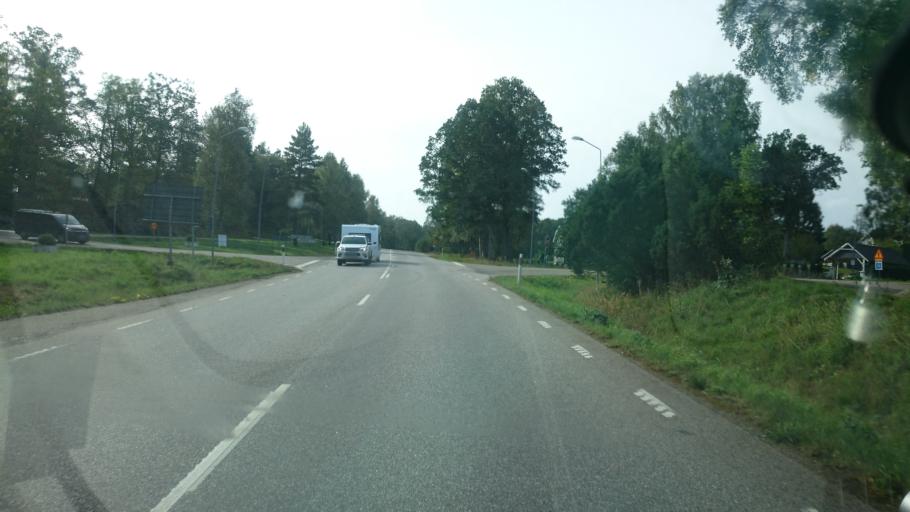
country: SE
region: Vaestra Goetaland
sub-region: Alingsas Kommun
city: Sollebrunn
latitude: 58.0828
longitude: 12.4885
